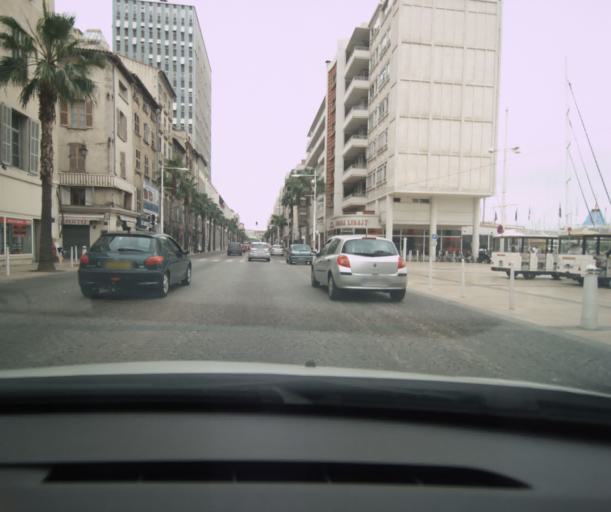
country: FR
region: Provence-Alpes-Cote d'Azur
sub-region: Departement du Var
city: Toulon
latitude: 43.1208
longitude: 5.9312
